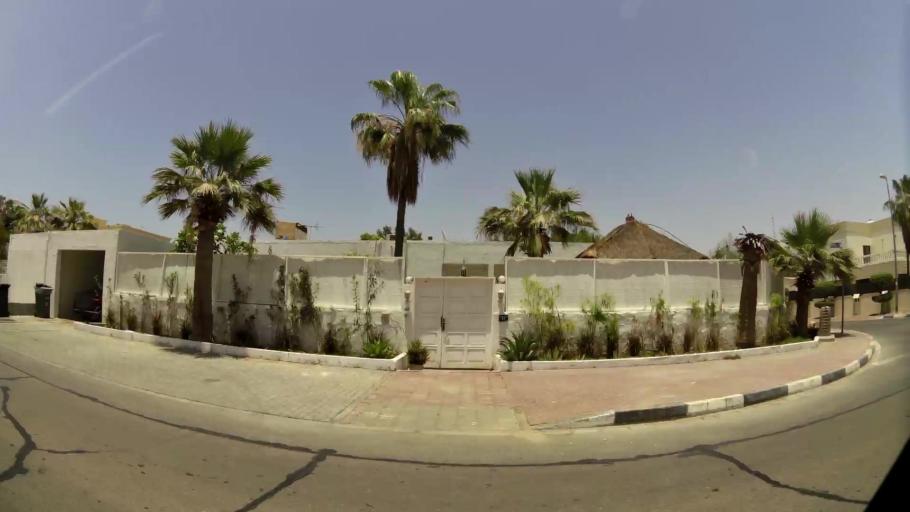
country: AE
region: Dubai
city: Dubai
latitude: 25.2189
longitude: 55.2577
